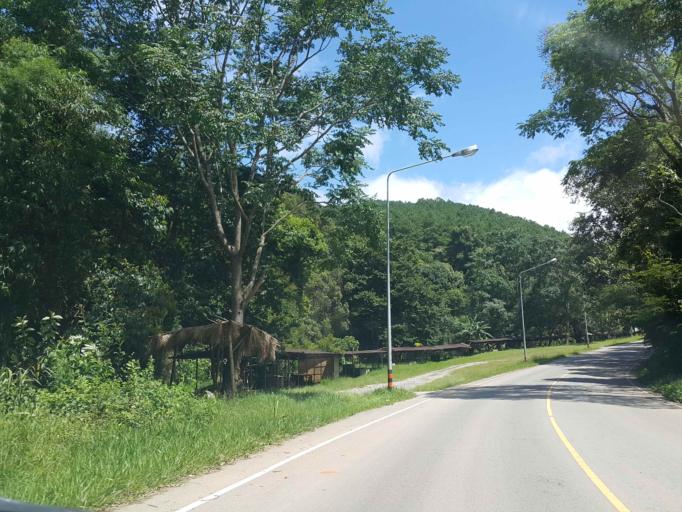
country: TH
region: Chiang Mai
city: Mae Chaem
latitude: 18.5294
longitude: 98.5230
